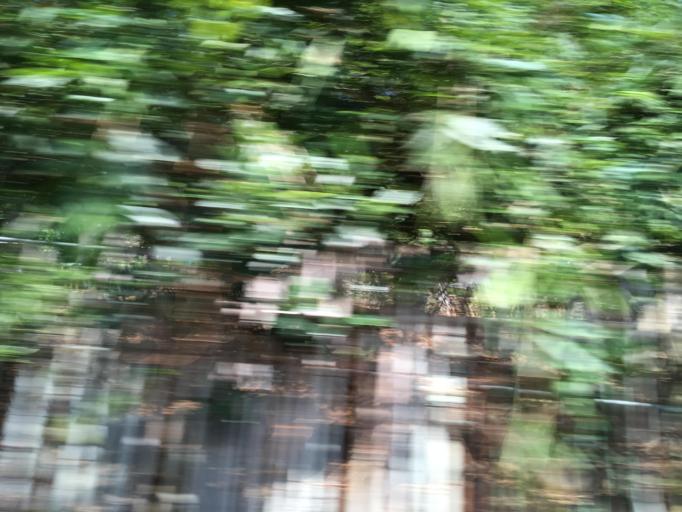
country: TW
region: Taipei
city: Taipei
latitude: 25.1536
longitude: 121.5027
